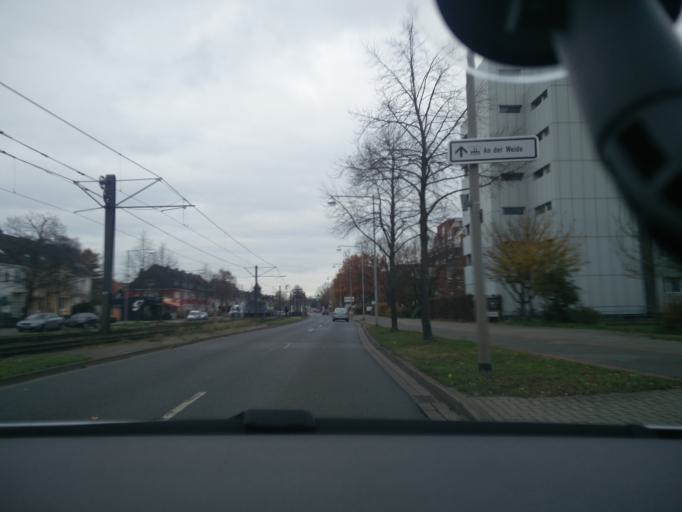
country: DE
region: Lower Saxony
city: Hannover
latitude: 52.3639
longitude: 9.7748
